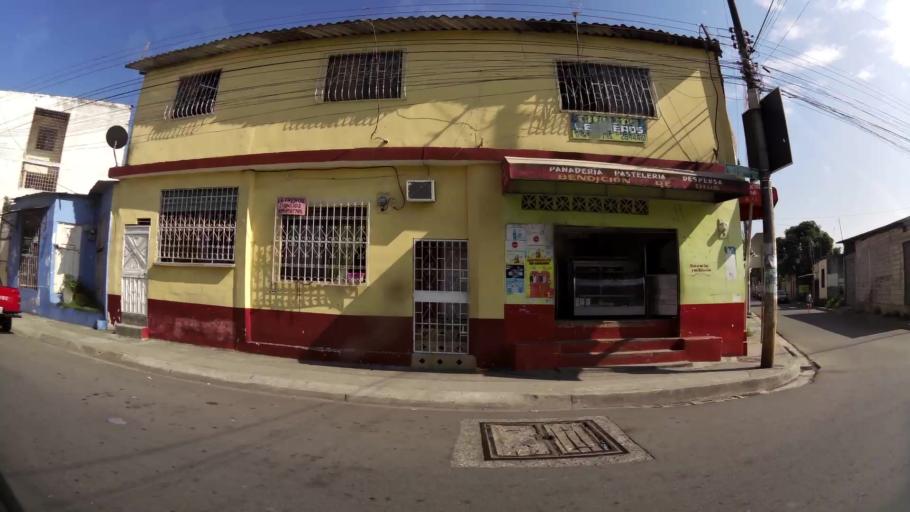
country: EC
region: Guayas
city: Eloy Alfaro
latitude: -2.0904
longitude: -79.9163
